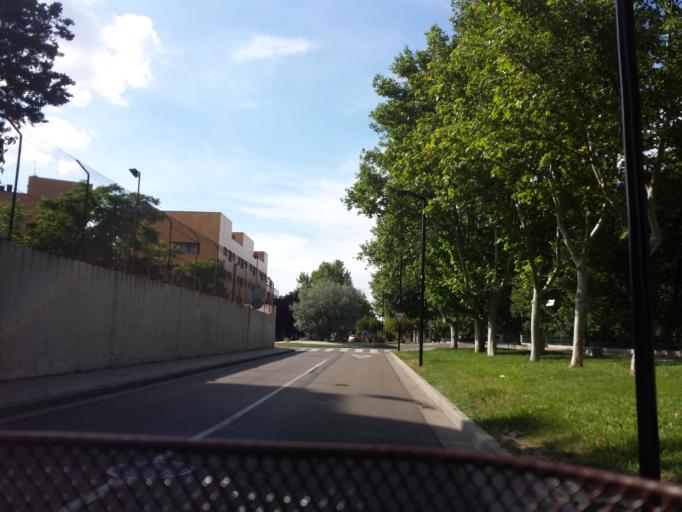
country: ES
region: Aragon
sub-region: Provincia de Zaragoza
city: Delicias
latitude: 41.6290
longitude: -0.9103
